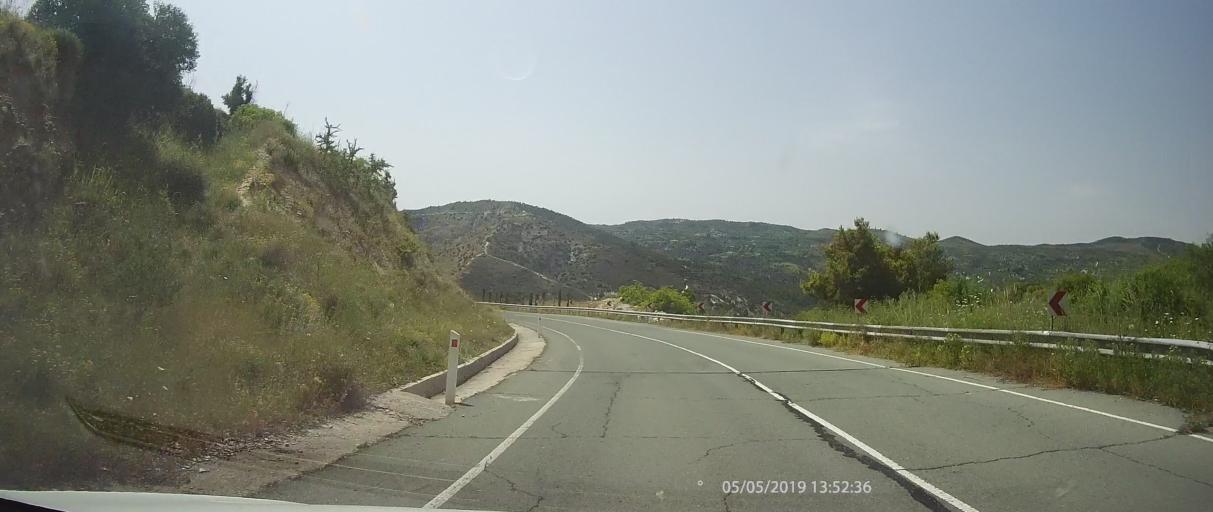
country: CY
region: Limassol
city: Pachna
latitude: 34.8285
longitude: 32.7310
